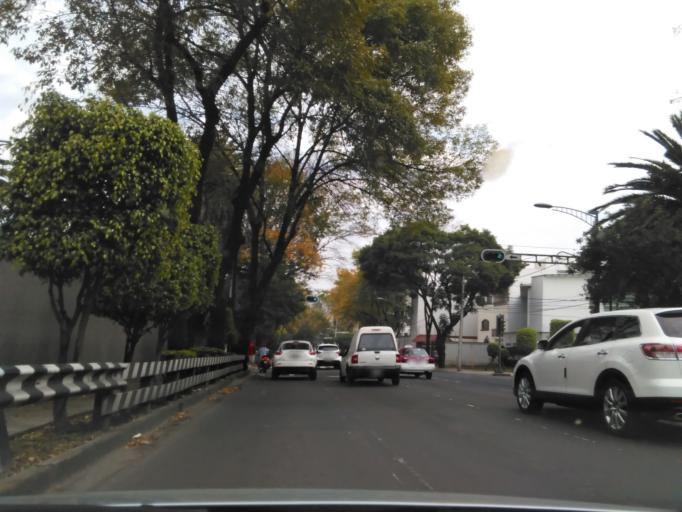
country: MX
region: Mexico City
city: Colonia del Valle
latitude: 19.3839
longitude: -99.1745
